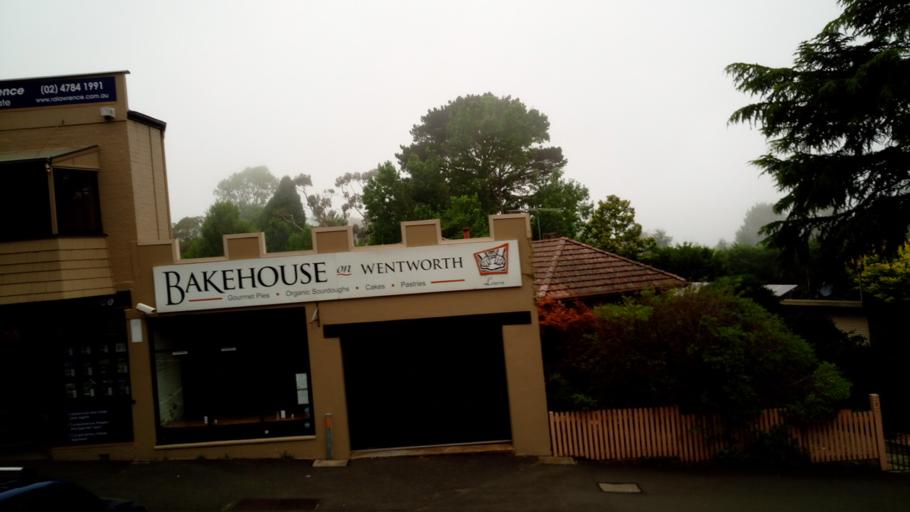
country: AU
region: New South Wales
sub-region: Blue Mountains Municipality
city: Leura
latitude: -33.7149
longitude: 150.3302
